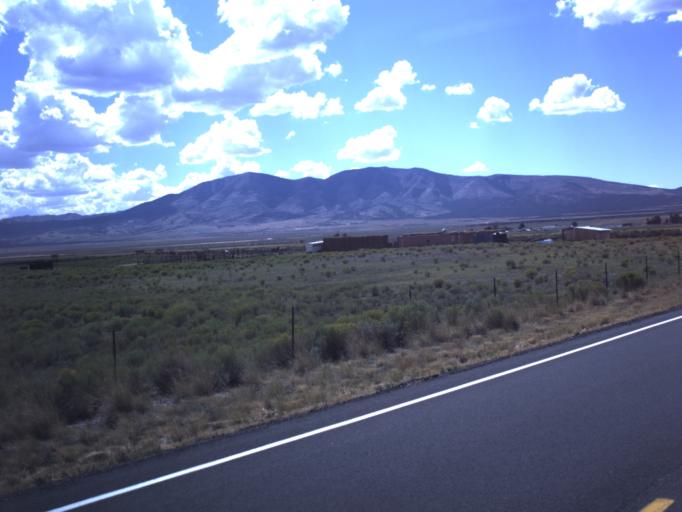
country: US
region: Utah
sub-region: Tooele County
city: Tooele
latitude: 40.3369
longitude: -112.4204
